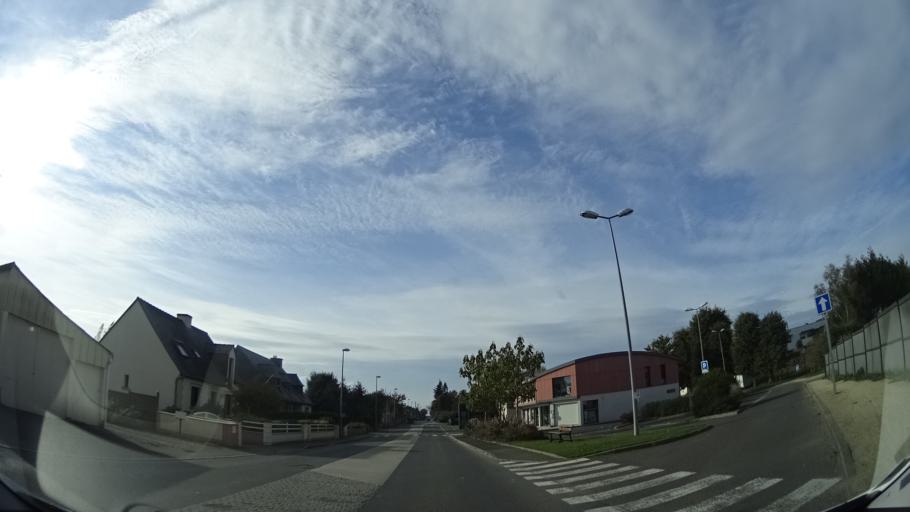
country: FR
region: Brittany
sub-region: Departement d'Ille-et-Vilaine
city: Romille
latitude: 48.2152
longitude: -1.8941
